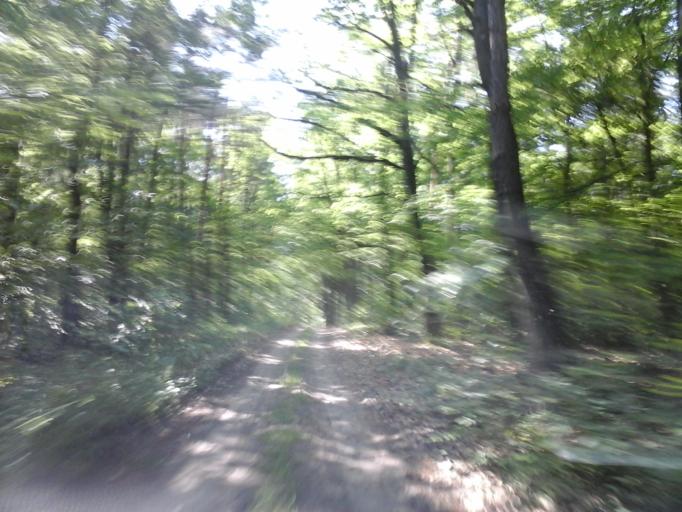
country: PL
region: West Pomeranian Voivodeship
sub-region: Powiat choszczenski
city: Bierzwnik
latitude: 53.0283
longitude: 15.6664
